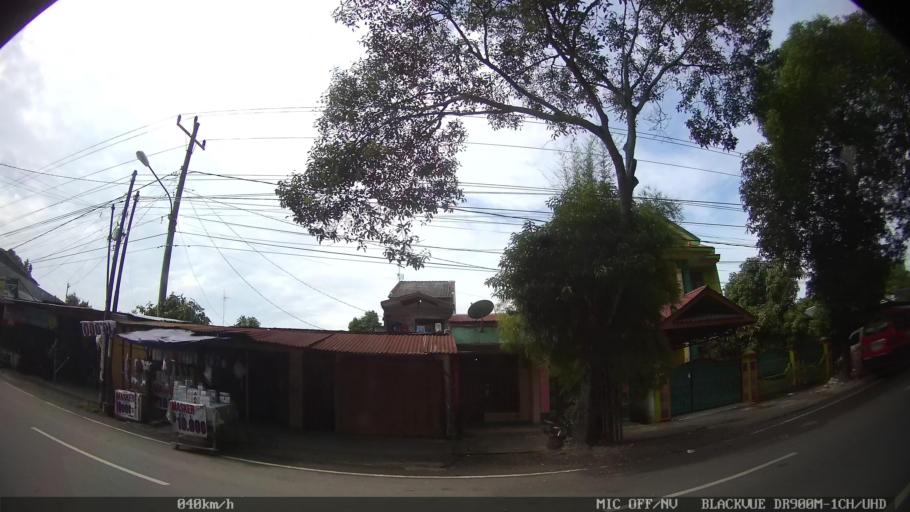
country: ID
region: North Sumatra
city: Medan
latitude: 3.6225
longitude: 98.6940
